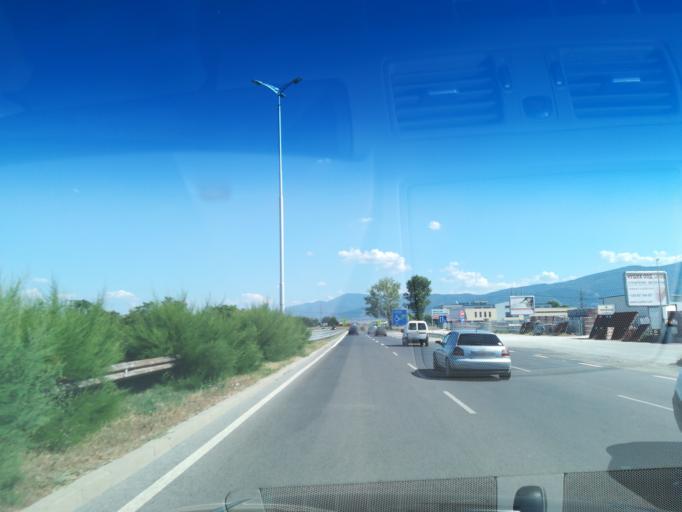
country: BG
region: Plovdiv
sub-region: Obshtina Plovdiv
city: Plovdiv
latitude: 42.1022
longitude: 24.7862
